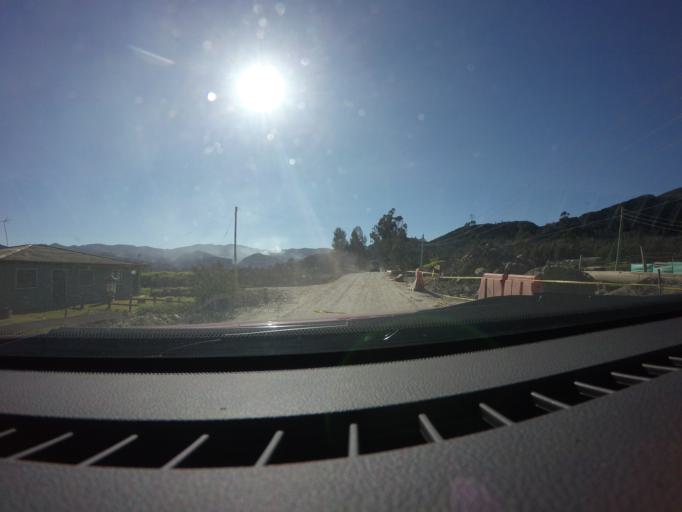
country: CO
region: Cundinamarca
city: Cucunuba
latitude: 5.2683
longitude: -73.7957
